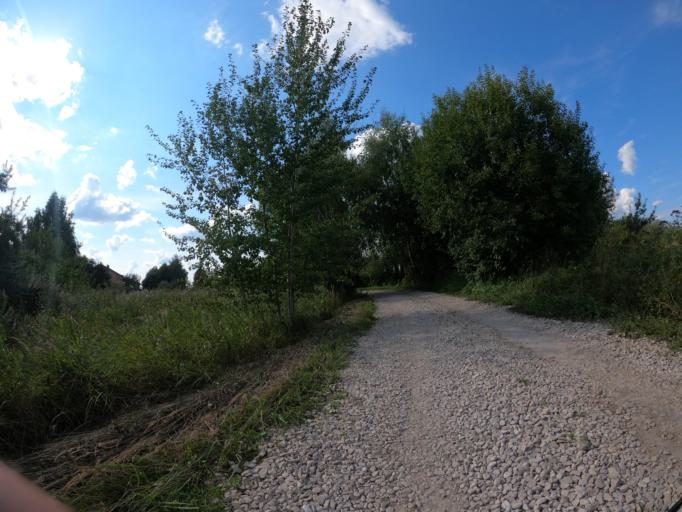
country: RU
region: Moskovskaya
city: Troitskoye
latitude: 55.2408
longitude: 38.4875
